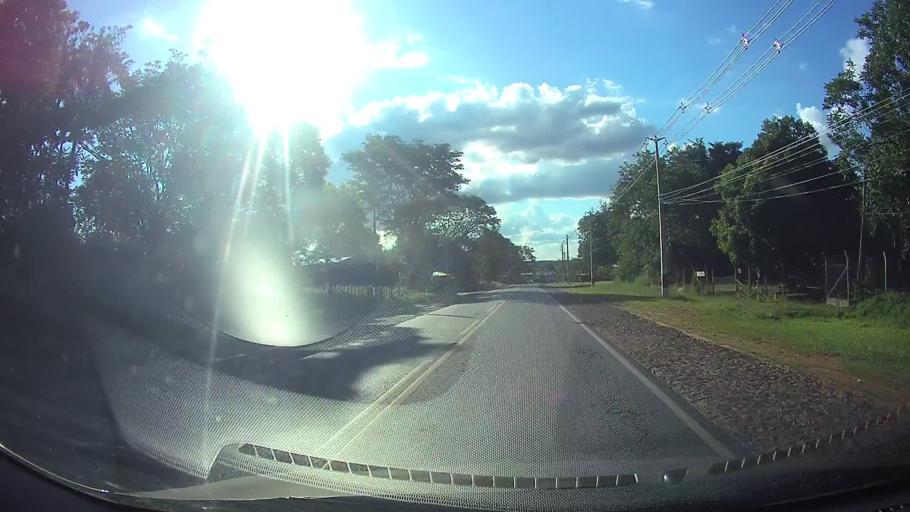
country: PY
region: Central
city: Aregua
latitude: -25.2955
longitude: -57.4312
